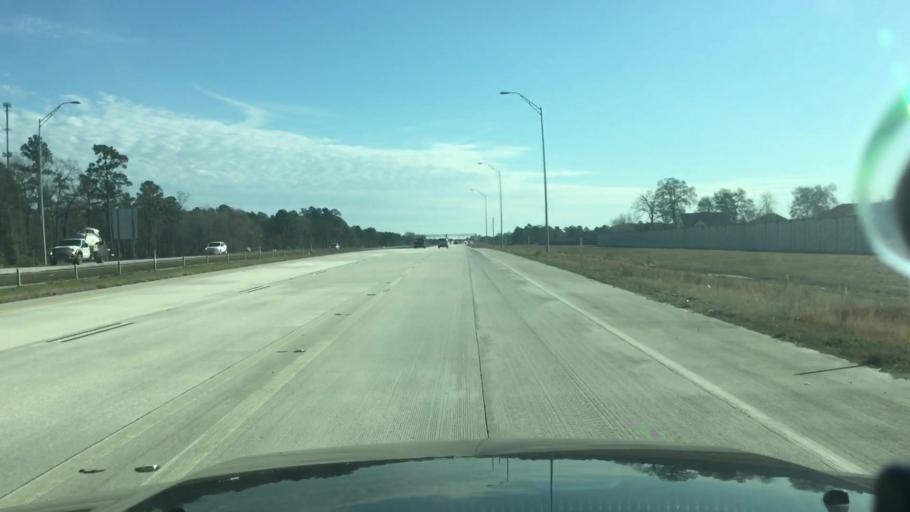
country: US
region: Texas
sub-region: Montgomery County
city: Porter Heights
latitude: 30.1376
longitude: -95.2852
